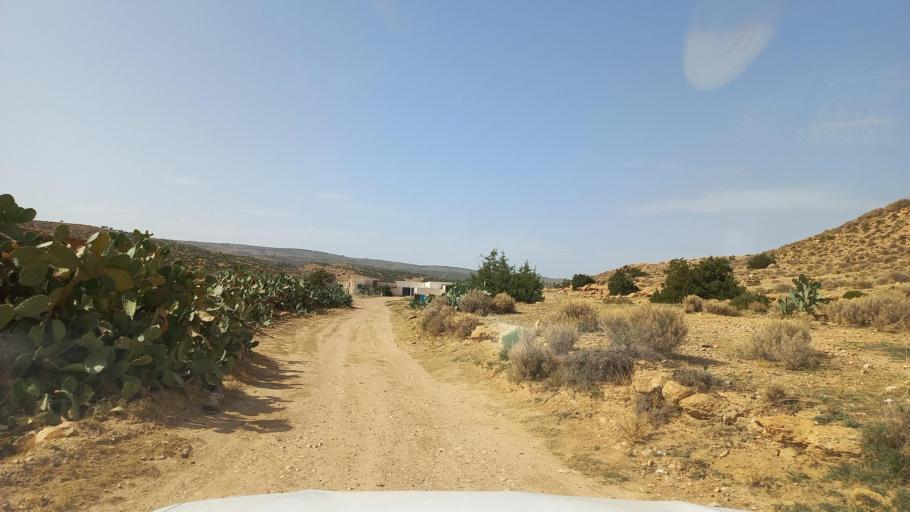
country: TN
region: Al Qasrayn
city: Kasserine
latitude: 35.3070
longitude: 8.9407
